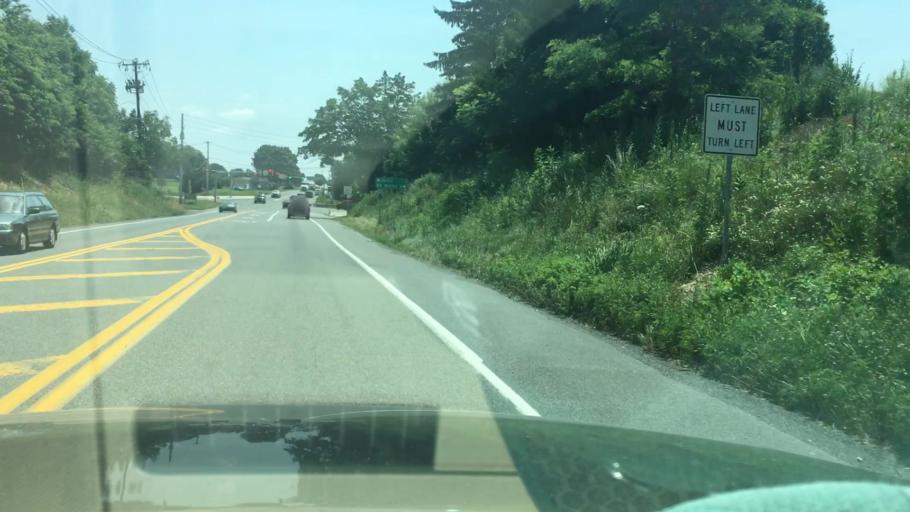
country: US
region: Pennsylvania
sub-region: Lehigh County
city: Schnecksville
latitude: 40.6151
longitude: -75.6555
